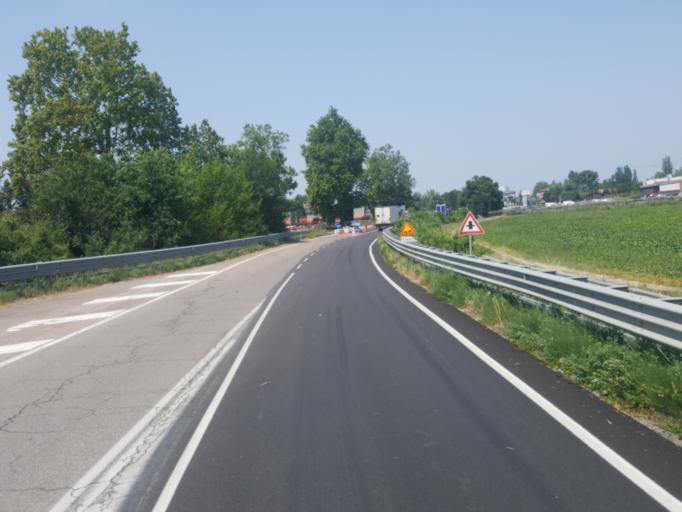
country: IT
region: Emilia-Romagna
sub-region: Provincia di Bologna
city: Anzola dell'Emilia
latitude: 44.5519
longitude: 11.1776
